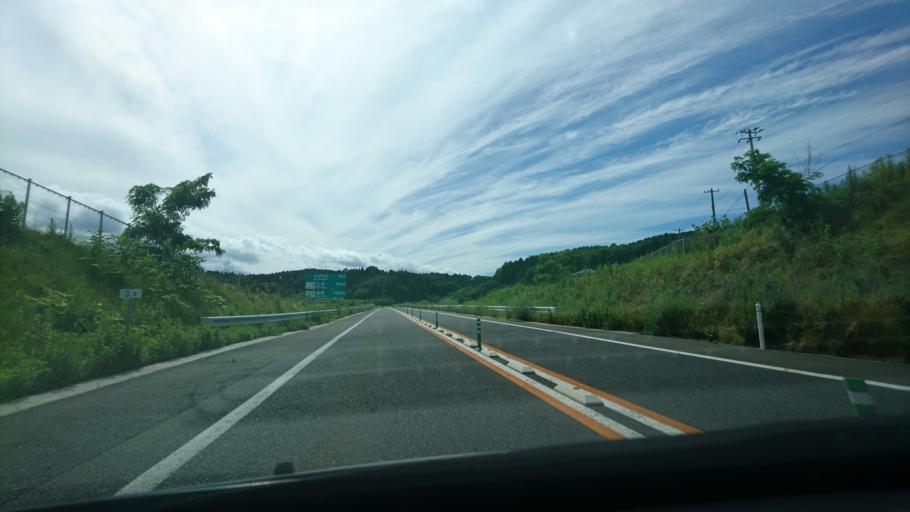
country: JP
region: Aomori
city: Hachinohe
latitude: 40.4793
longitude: 141.4944
